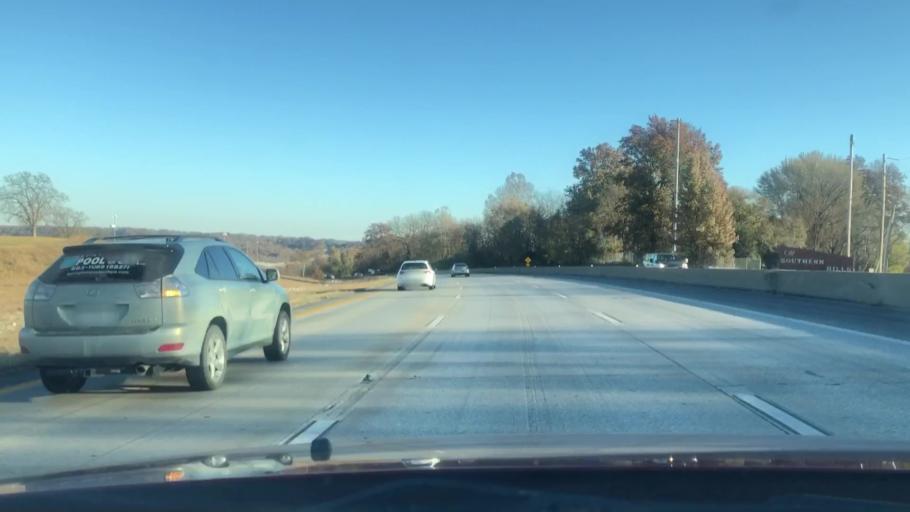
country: US
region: Missouri
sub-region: Greene County
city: Springfield
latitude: 37.1322
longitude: -93.2441
